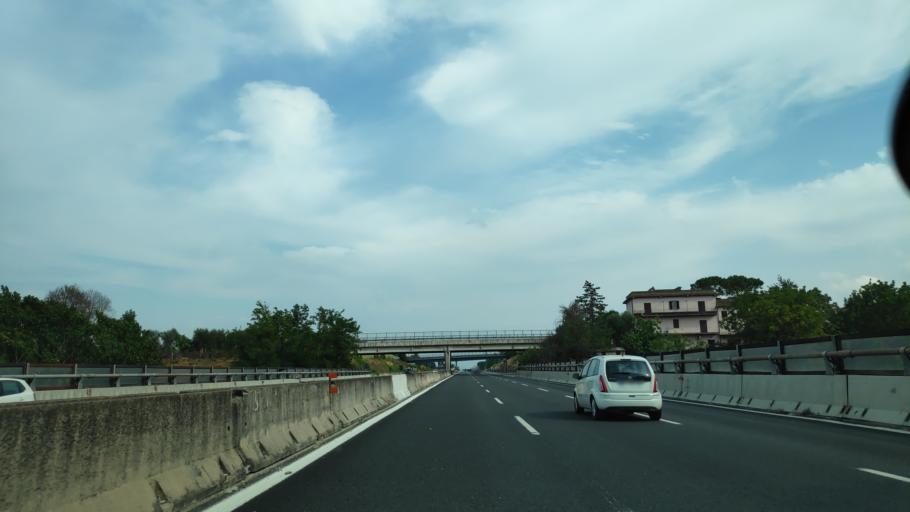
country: IT
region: Latium
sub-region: Citta metropolitana di Roma Capitale
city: Fiano Romano
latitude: 42.1762
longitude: 12.6054
